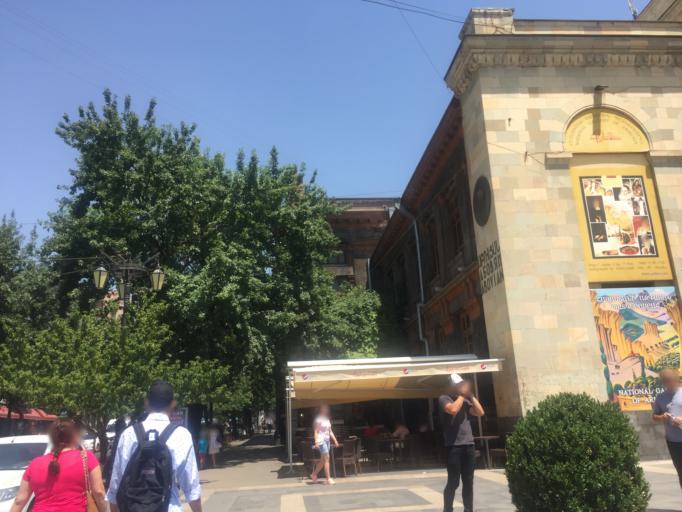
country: AM
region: Yerevan
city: Yerevan
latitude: 40.1788
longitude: 44.5133
